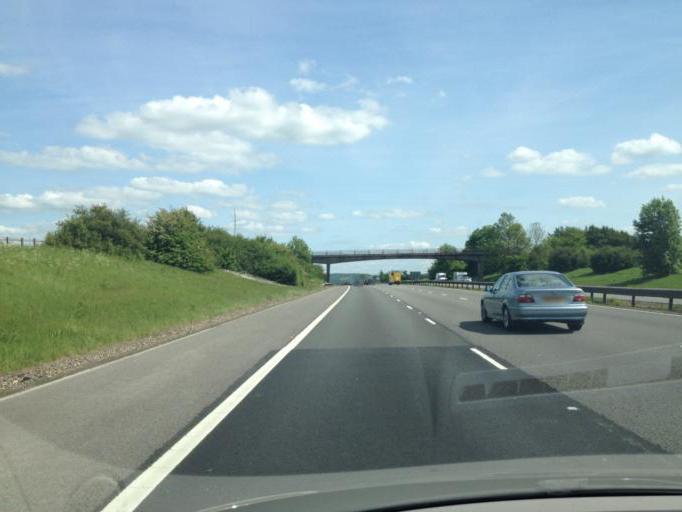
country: GB
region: England
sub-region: Oxfordshire
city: Thame
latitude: 51.7116
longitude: -1.0158
